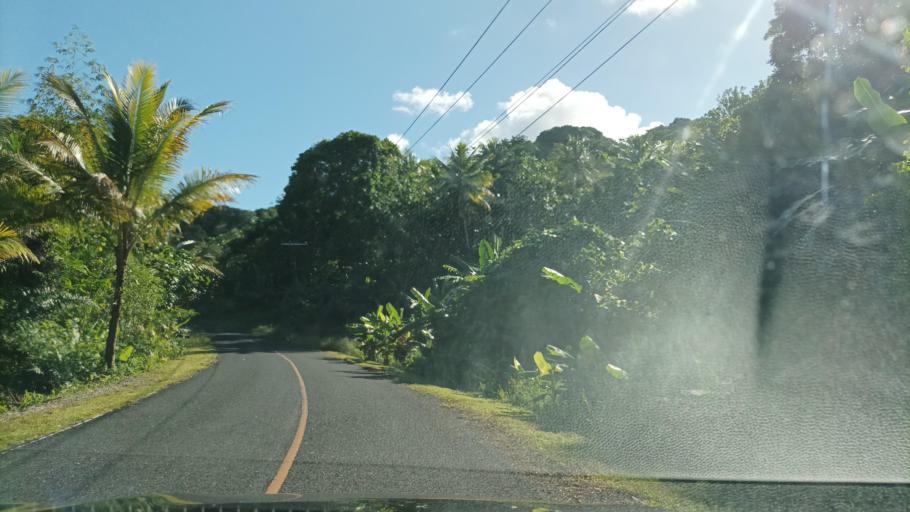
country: FM
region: Pohnpei
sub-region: Madolenihm Municipality
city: Madolenihm Municipality Government
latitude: 6.8062
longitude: 158.2708
